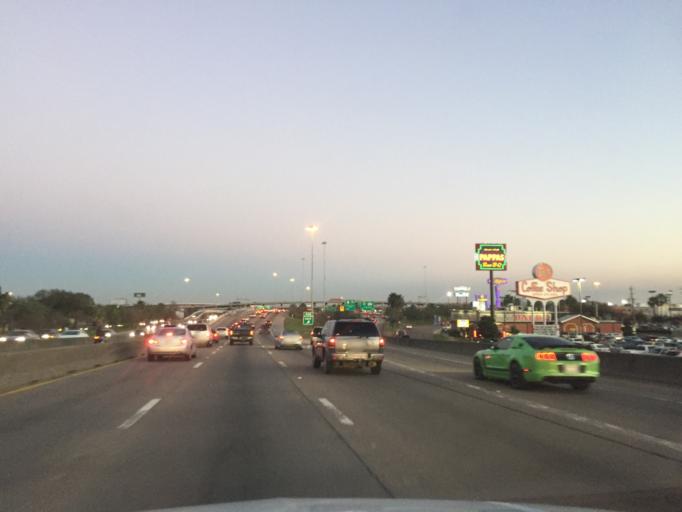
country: US
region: Texas
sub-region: Harris County
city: South Houston
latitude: 29.7017
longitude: -95.2952
